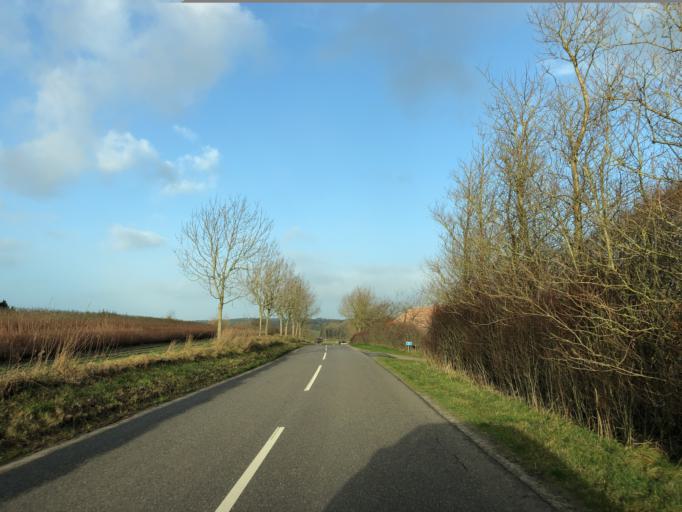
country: DK
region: Central Jutland
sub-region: Ringkobing-Skjern Kommune
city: Videbaek
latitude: 56.1918
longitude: 8.5421
